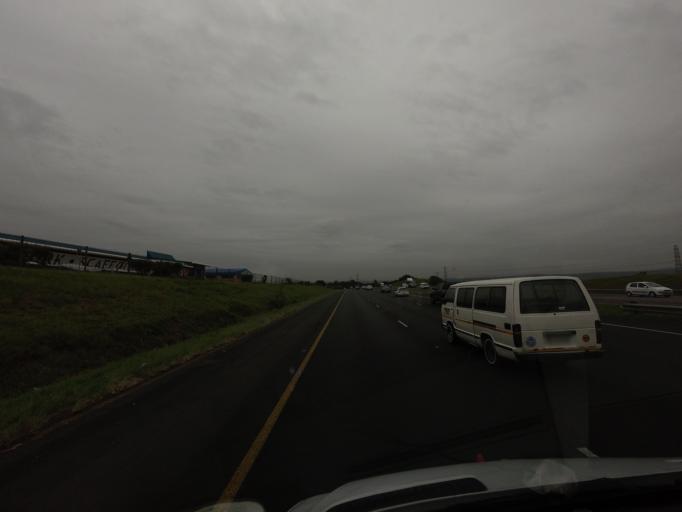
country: ZA
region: KwaZulu-Natal
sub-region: eThekwini Metropolitan Municipality
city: Durban
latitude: -29.7488
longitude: 31.0315
